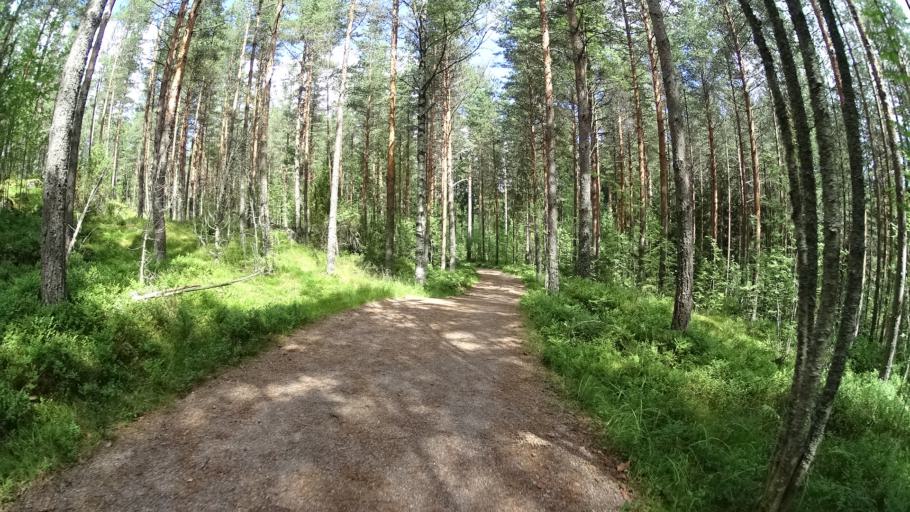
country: FI
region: Uusimaa
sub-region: Helsinki
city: Kauniainen
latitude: 60.3192
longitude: 24.6816
